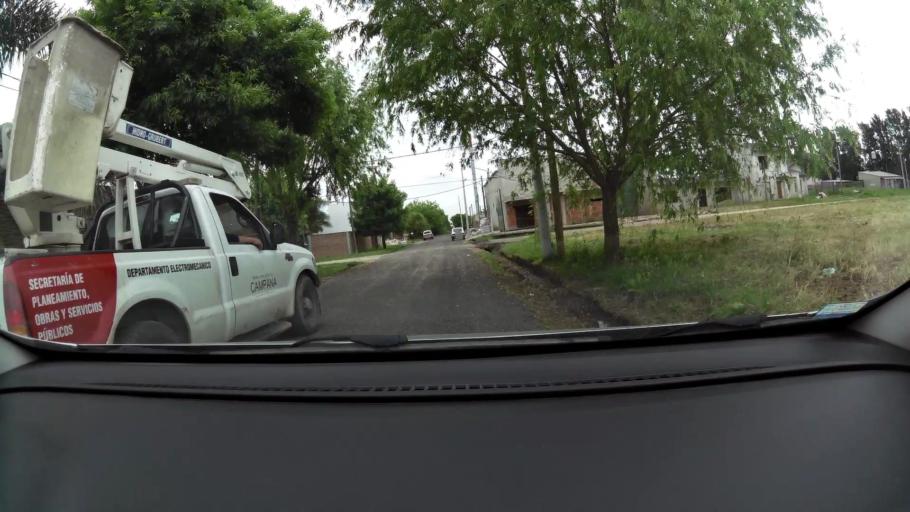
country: AR
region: Buenos Aires
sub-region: Partido de Campana
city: Campana
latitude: -34.1981
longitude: -58.9475
